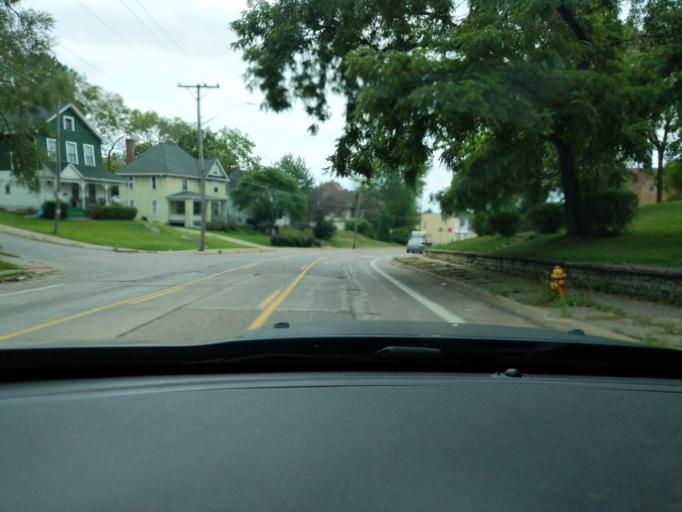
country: US
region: Iowa
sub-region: Scott County
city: Davenport
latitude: 41.5291
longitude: -90.5911
